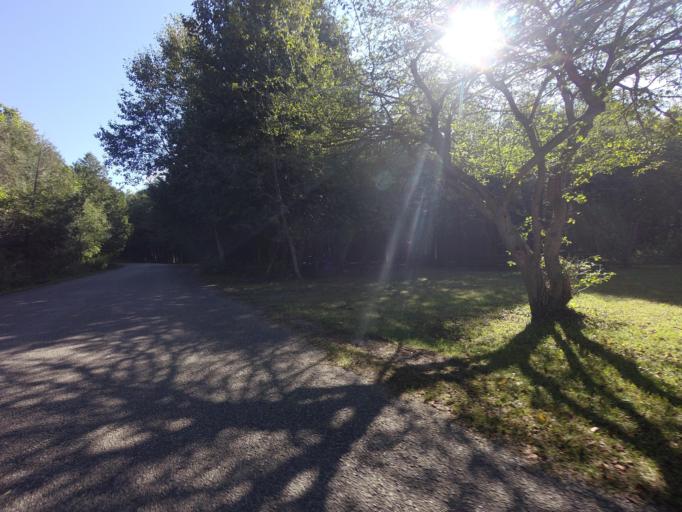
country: CA
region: Ontario
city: Waterloo
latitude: 43.6737
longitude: -80.4502
